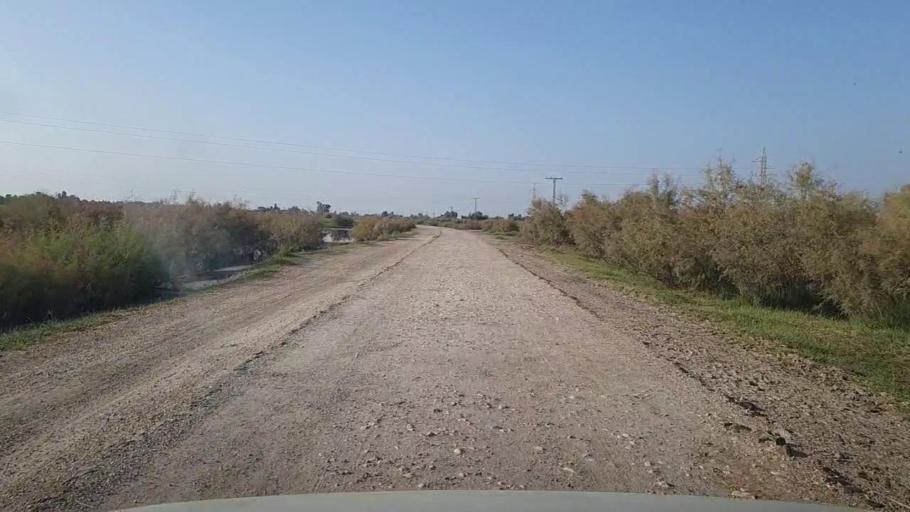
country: PK
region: Sindh
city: Kandhkot
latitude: 28.3058
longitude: 69.3287
